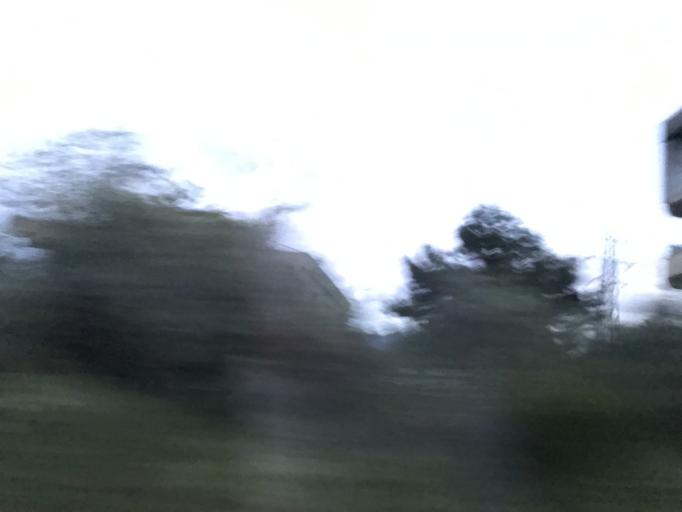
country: TR
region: Hatay
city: Karacay
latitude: 36.1485
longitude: 36.0844
